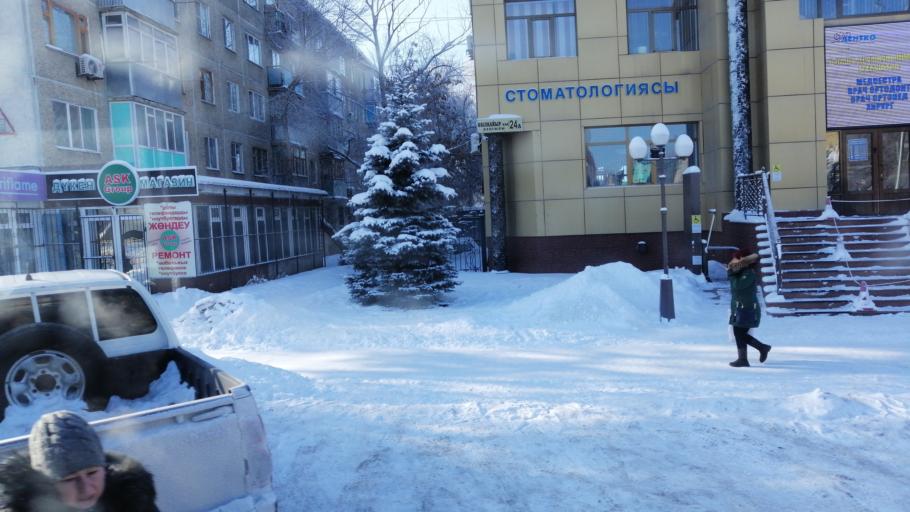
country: KZ
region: Aqtoebe
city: Aqtobe
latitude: 50.3048
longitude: 57.1512
